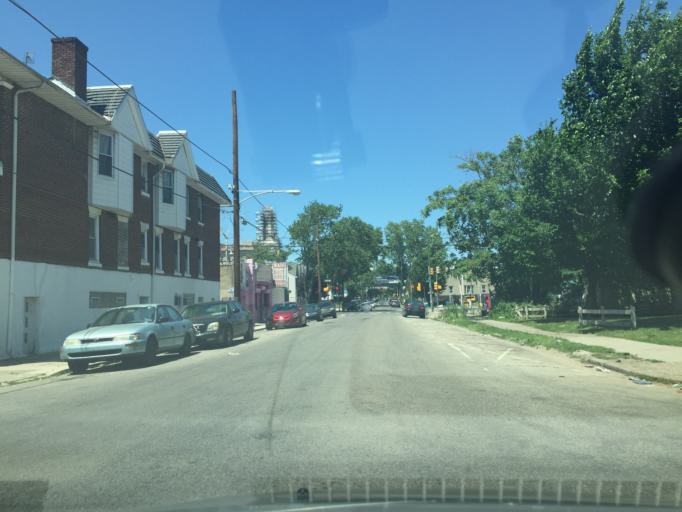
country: US
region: Pennsylvania
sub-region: Delaware County
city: Millbourne
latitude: 39.9563
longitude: -75.2145
